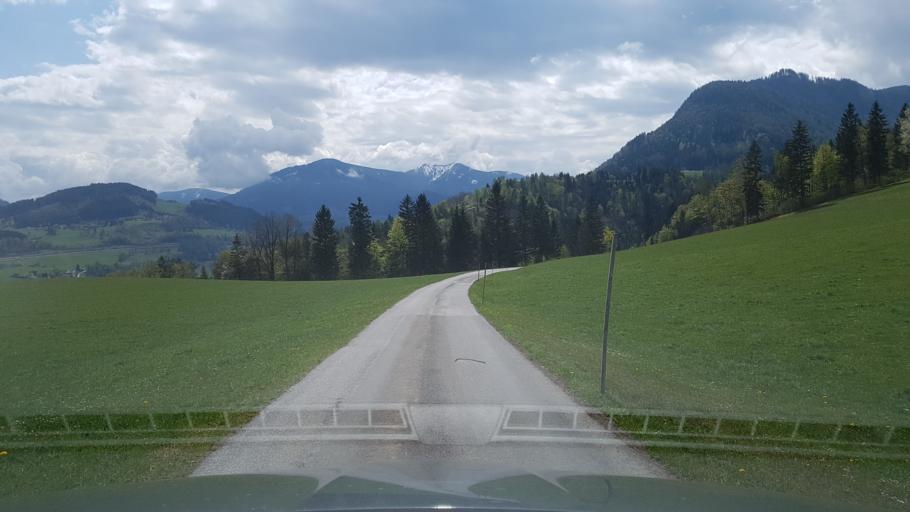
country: AT
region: Salzburg
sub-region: Politischer Bezirk Sankt Johann im Pongau
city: Werfen
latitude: 47.4635
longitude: 13.1876
